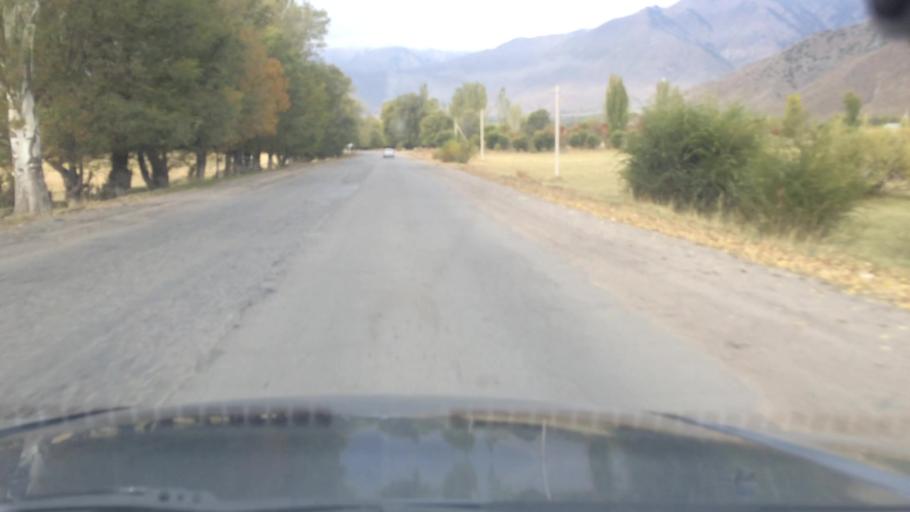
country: KG
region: Ysyk-Koel
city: Tyup
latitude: 42.7840
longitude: 78.2773
